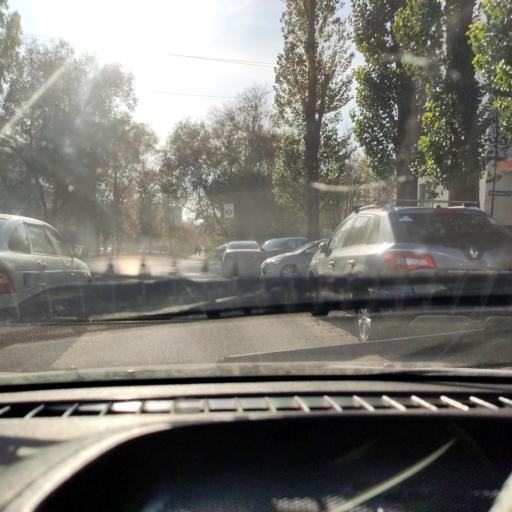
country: RU
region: Samara
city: Zhigulevsk
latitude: 53.4852
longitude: 49.4697
